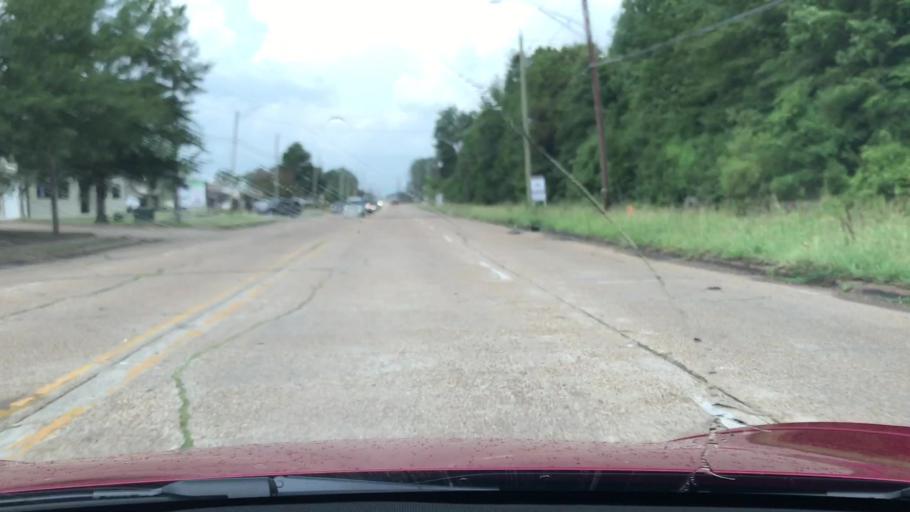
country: US
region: Louisiana
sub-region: Bossier Parish
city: Bossier City
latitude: 32.4096
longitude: -93.7632
